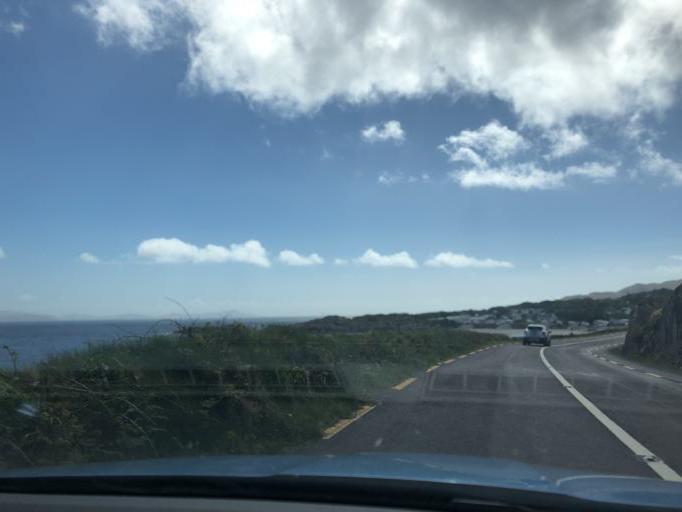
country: IE
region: Munster
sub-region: Ciarrai
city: Cahersiveen
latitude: 51.7614
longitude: -10.0756
